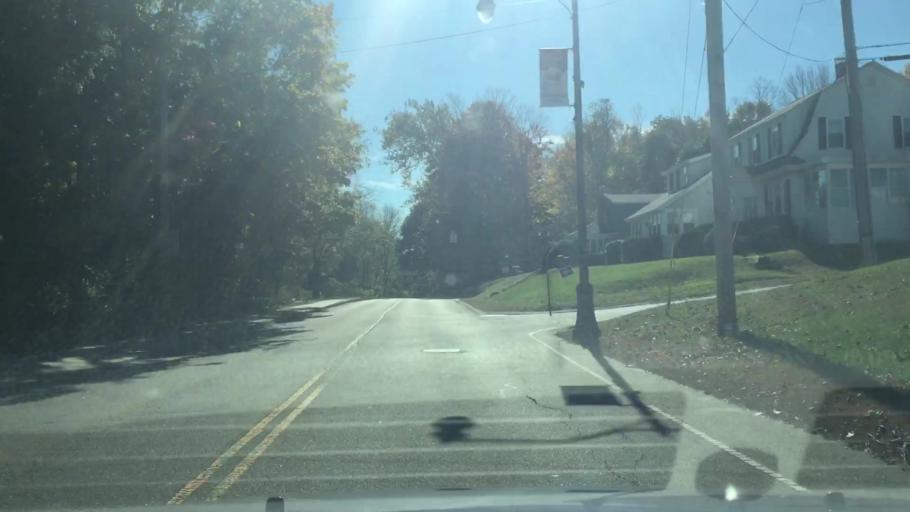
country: US
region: Massachusetts
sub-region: Essex County
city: North Andover
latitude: 42.6905
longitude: -71.1182
